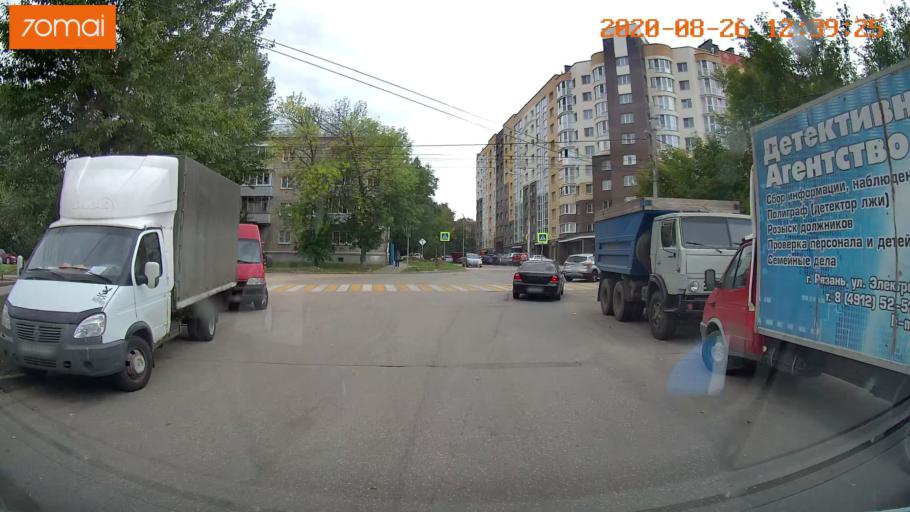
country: RU
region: Rjazan
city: Ryazan'
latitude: 54.6056
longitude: 39.7581
